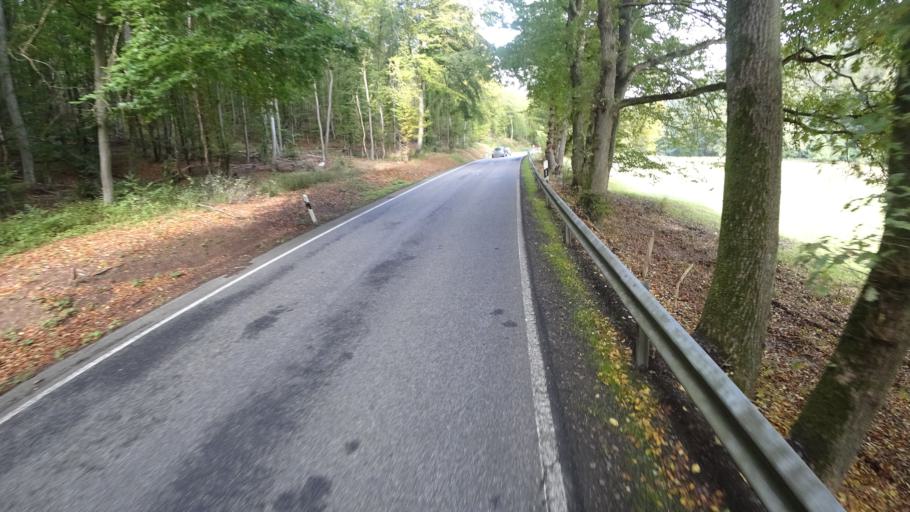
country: DE
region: Rheinland-Pfalz
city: Isselbach
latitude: 50.3921
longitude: 7.9071
